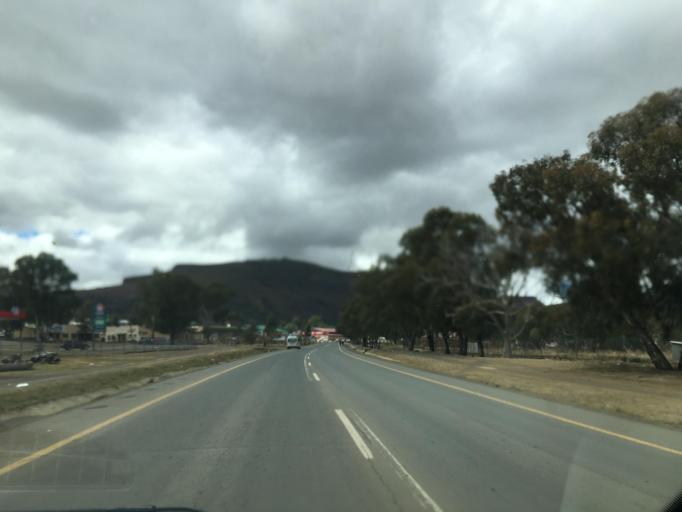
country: ZA
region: Eastern Cape
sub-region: Chris Hani District Municipality
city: Cala
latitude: -31.5273
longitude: 27.6899
